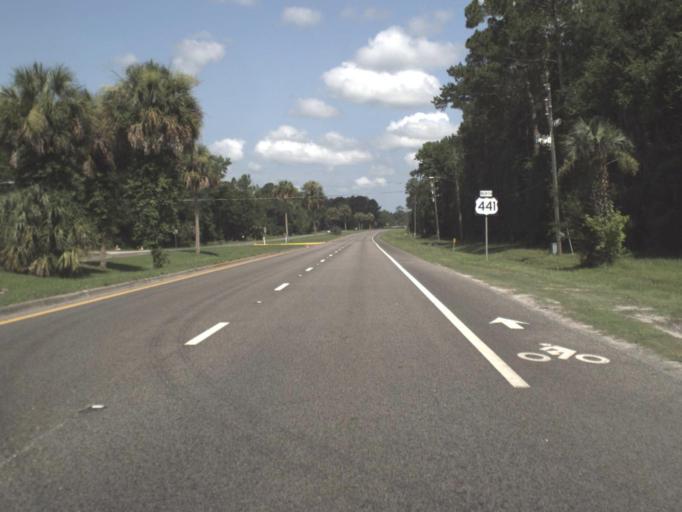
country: US
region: Florida
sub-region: Alachua County
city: Gainesville
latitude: 29.5115
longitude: -82.2801
